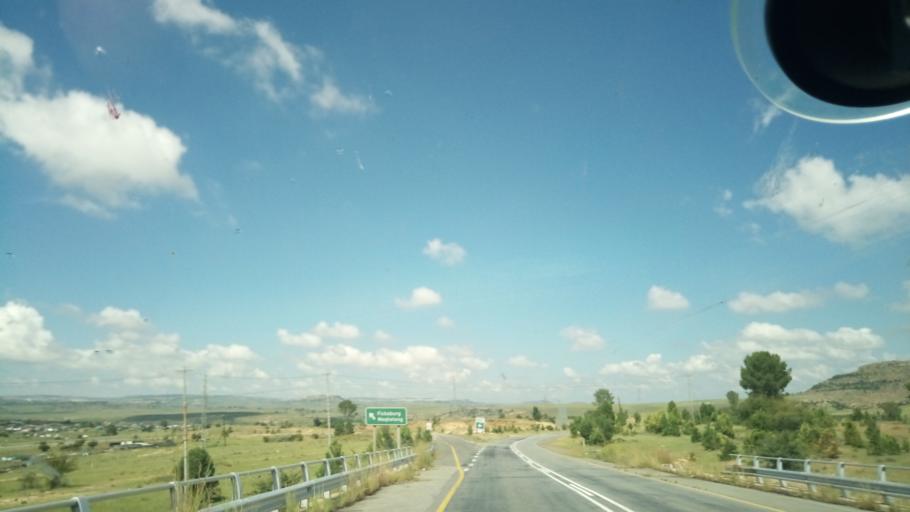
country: ZA
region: Orange Free State
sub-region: Thabo Mofutsanyana District Municipality
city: Ficksburg
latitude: -28.8870
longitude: 27.8635
